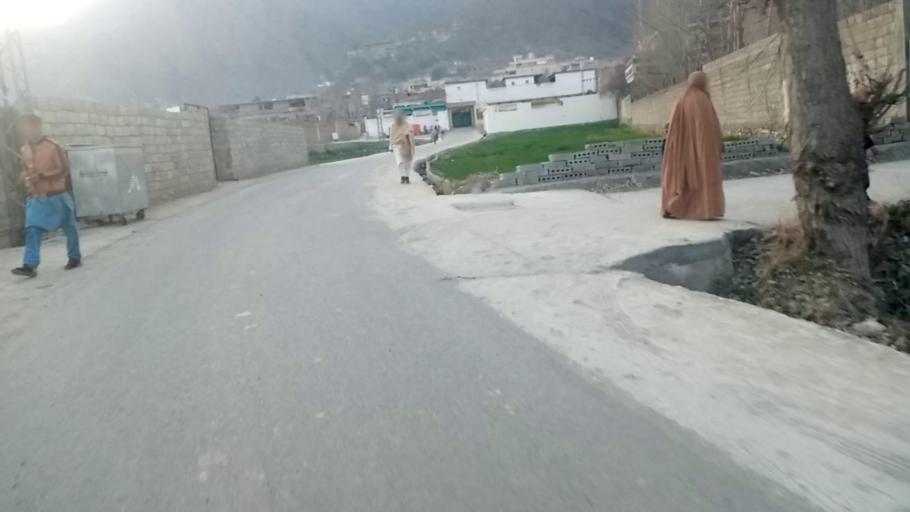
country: PK
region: Khyber Pakhtunkhwa
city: Saidu Sharif
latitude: 34.7404
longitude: 72.3387
